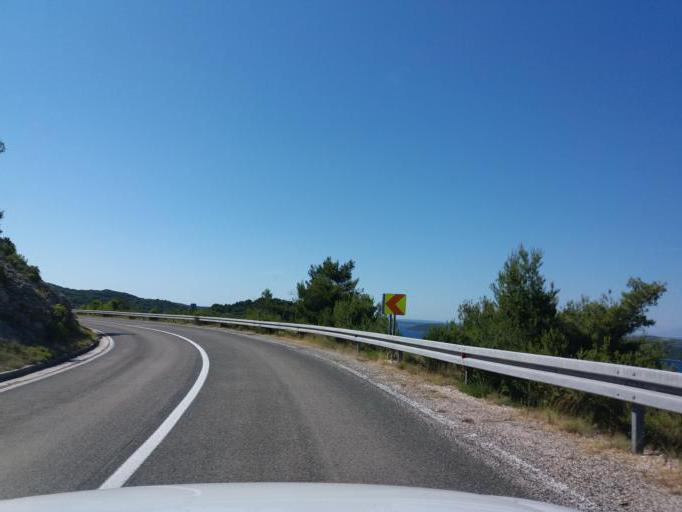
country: HR
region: Zadarska
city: Ugljan
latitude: 44.1189
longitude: 14.9215
